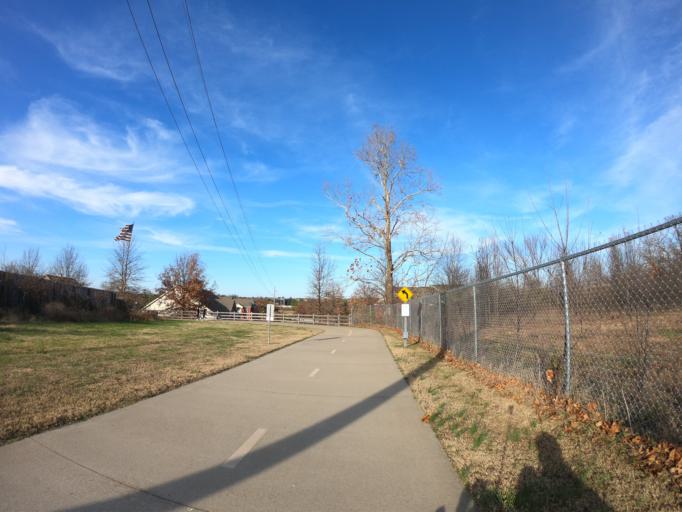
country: US
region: Arkansas
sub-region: Benton County
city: Lowell
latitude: 36.2906
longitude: -94.1652
